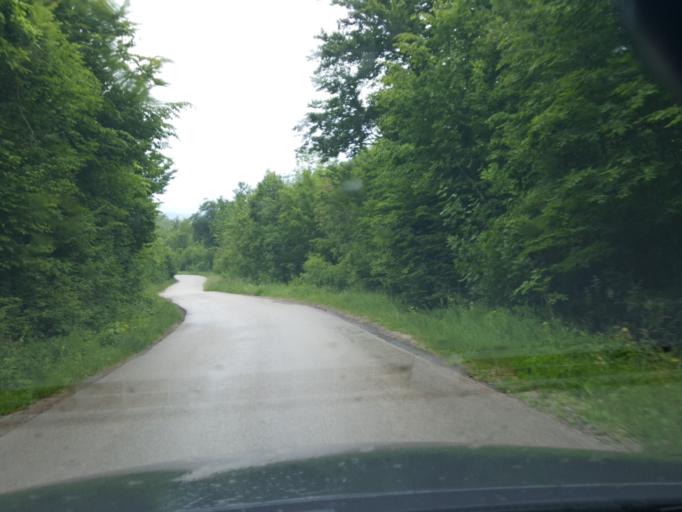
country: RS
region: Central Serbia
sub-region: Zajecarski Okrug
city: Boljevac
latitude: 43.7886
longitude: 21.9130
